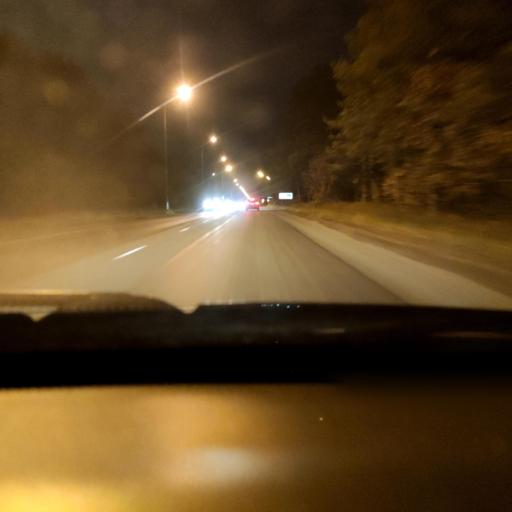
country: RU
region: Perm
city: Perm
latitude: 58.0635
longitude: 56.2667
